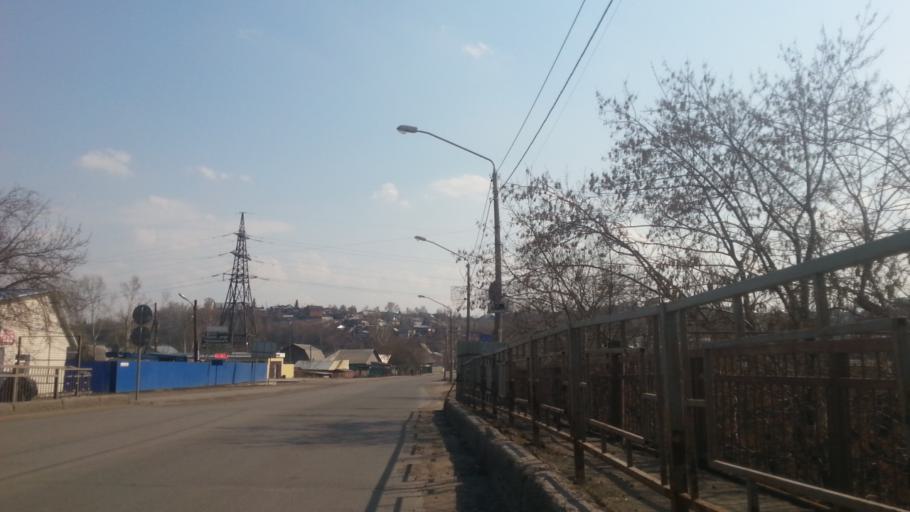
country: RU
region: Altai Krai
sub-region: Gorod Barnaulskiy
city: Barnaul
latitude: 53.3225
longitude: 83.7681
